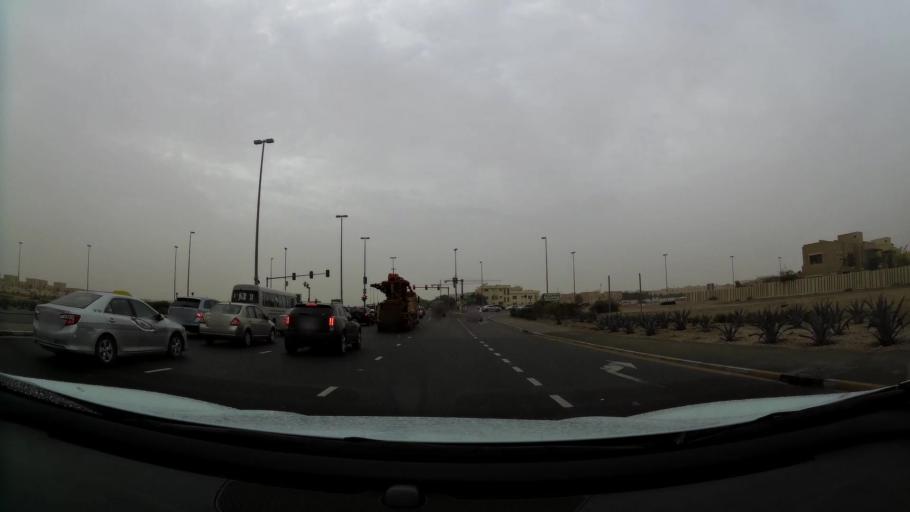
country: AE
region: Abu Dhabi
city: Abu Dhabi
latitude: 24.4419
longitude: 54.6012
